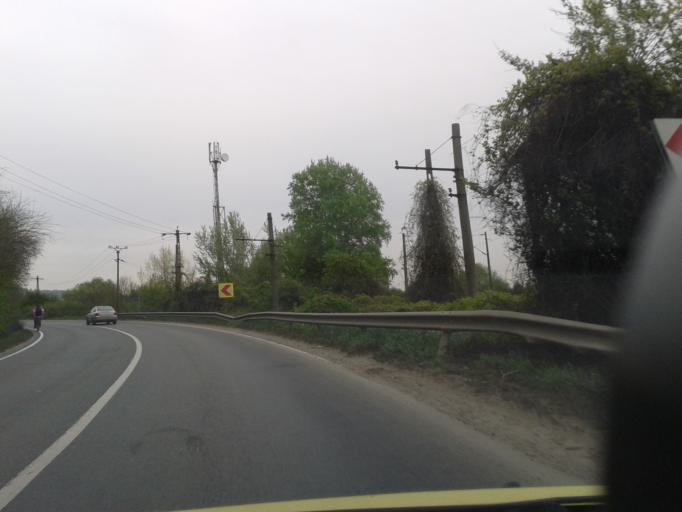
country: RO
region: Arad
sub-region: Comuna Zabrani
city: Neudorf
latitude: 46.1032
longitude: 21.6406
